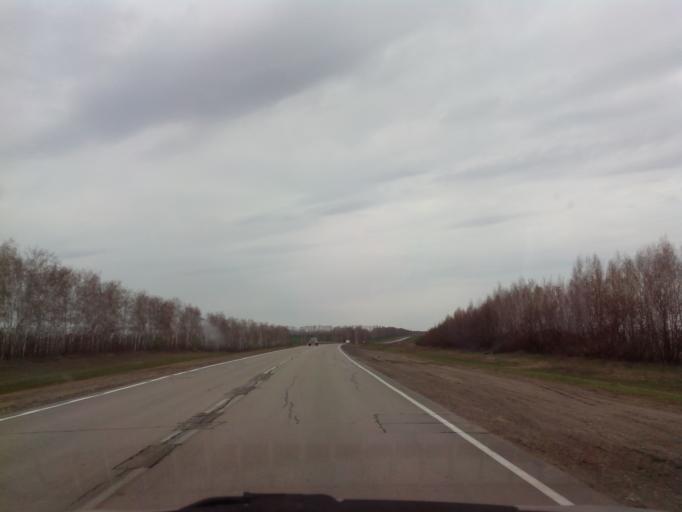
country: RU
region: Tambov
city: Znamenka
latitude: 52.4153
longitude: 41.3783
